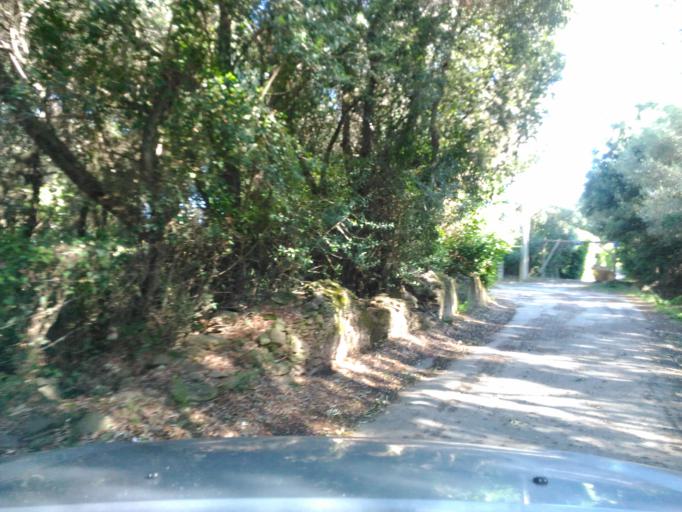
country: FR
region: Corsica
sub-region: Departement de la Haute-Corse
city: Brando
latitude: 42.9627
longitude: 9.4481
